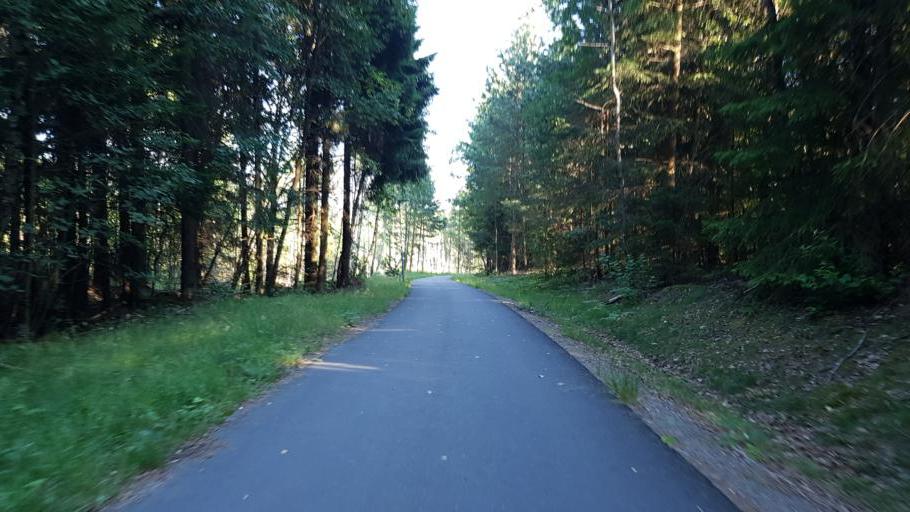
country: SE
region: Vaestra Goetaland
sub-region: Harryda Kommun
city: Molnlycke
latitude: 57.6741
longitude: 12.0966
